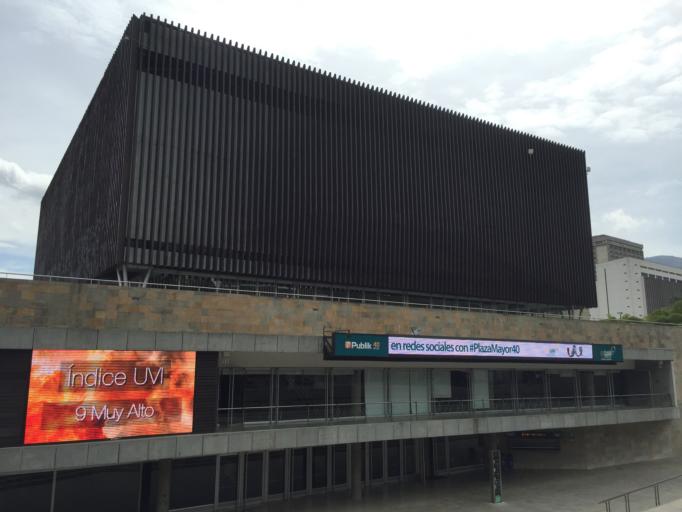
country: CO
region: Antioquia
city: Medellin
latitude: 6.2426
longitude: -75.5766
